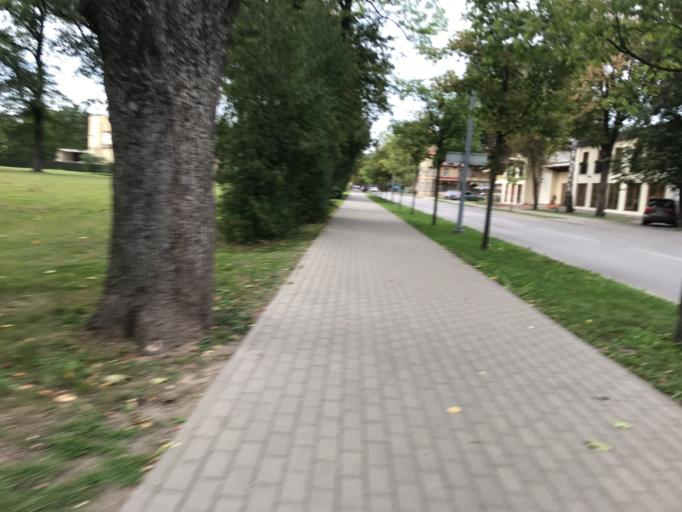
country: LT
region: Alytaus apskritis
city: Druskininkai
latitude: 54.0219
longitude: 23.9706
